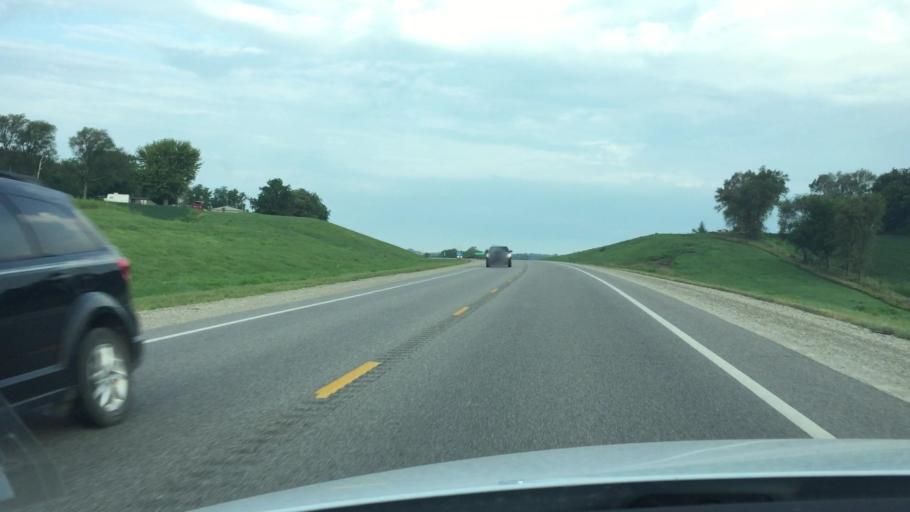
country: US
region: Kansas
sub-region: Doniphan County
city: Troy
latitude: 39.7939
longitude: -95.0806
